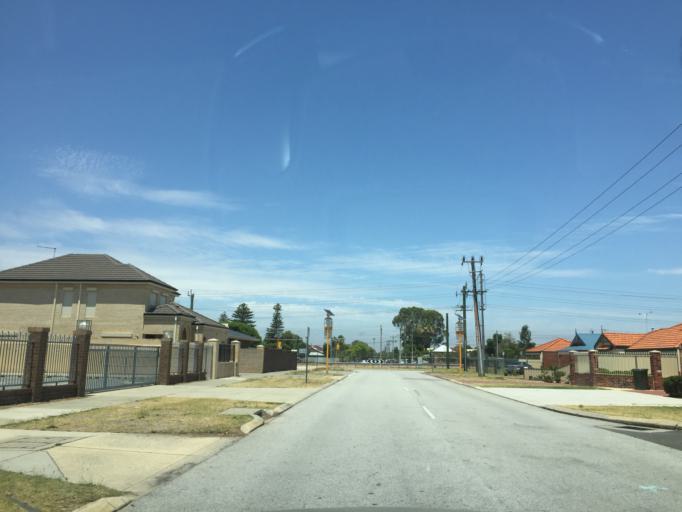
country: AU
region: Western Australia
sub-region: Canning
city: Queens Park
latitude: -32.0051
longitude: 115.9378
